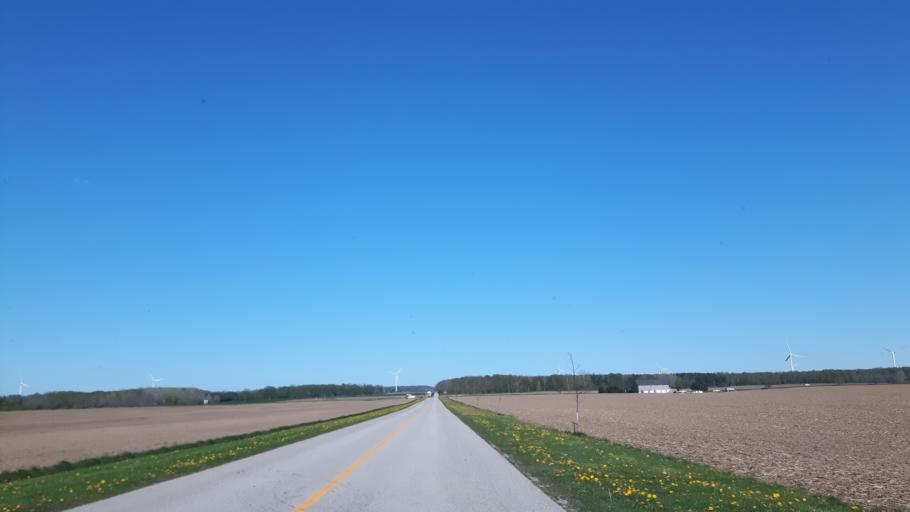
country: CA
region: Ontario
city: Bluewater
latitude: 43.5106
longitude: -81.7024
